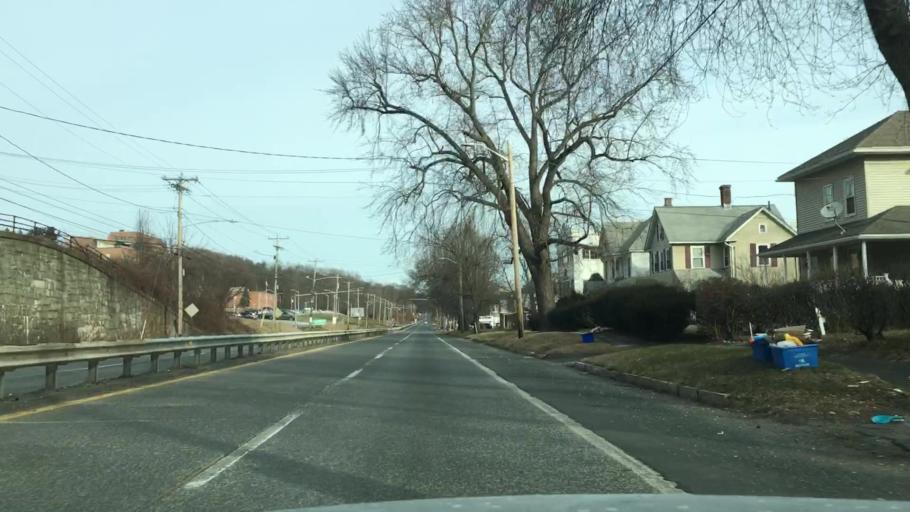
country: US
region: Massachusetts
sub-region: Hampden County
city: Chicopee
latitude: 42.1628
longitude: -72.6330
